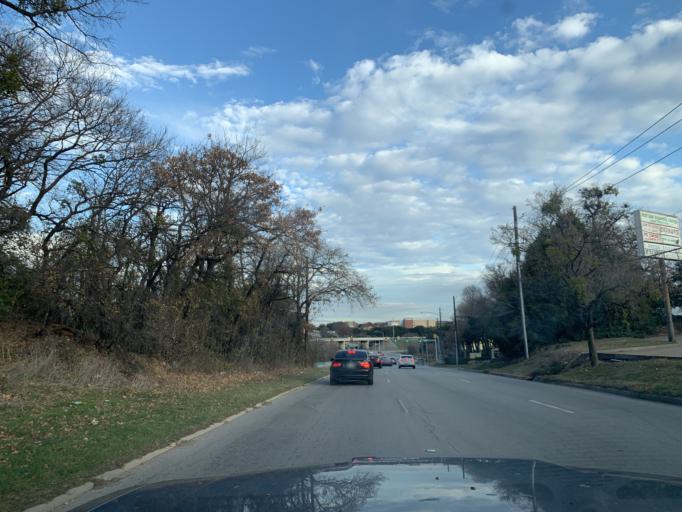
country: US
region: Texas
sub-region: Tarrant County
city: Euless
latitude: 32.8226
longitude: -97.0662
